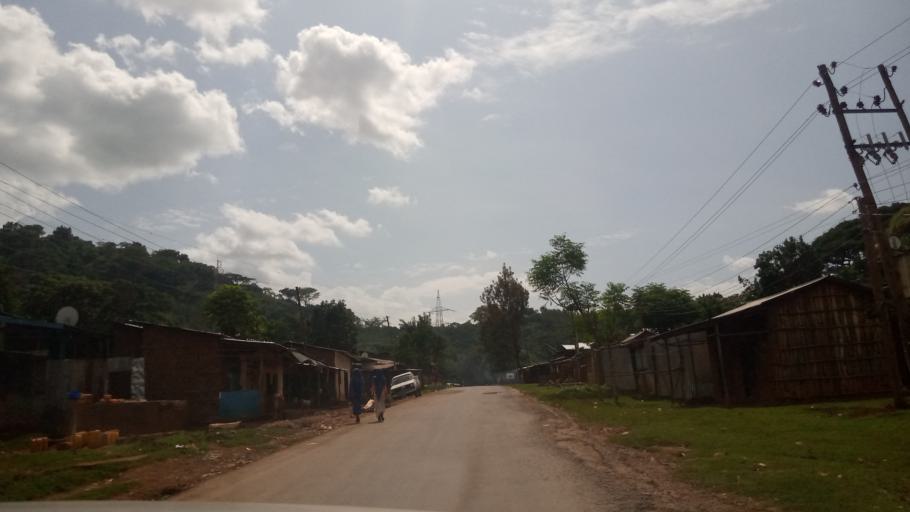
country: ET
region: Oromiya
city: Agaro
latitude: 7.9211
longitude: 36.5192
